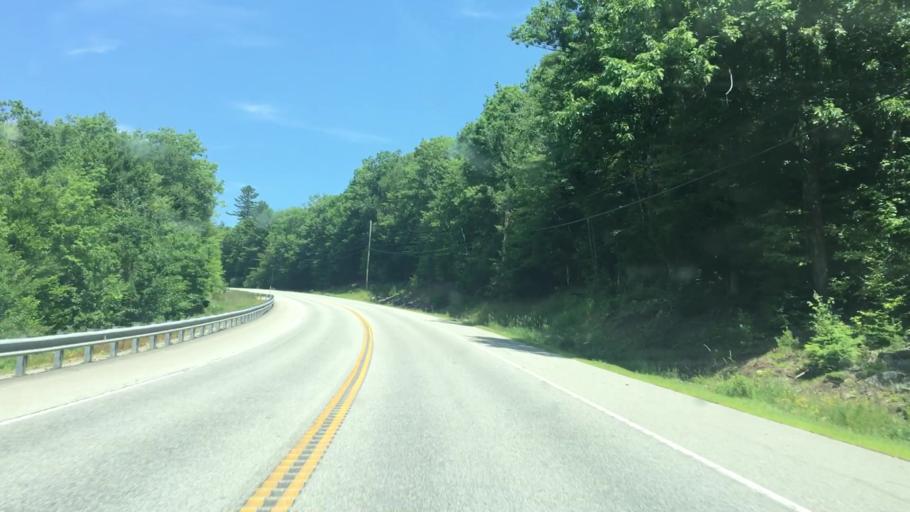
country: US
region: Maine
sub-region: Androscoggin County
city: Livermore
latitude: 44.4140
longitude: -70.2206
